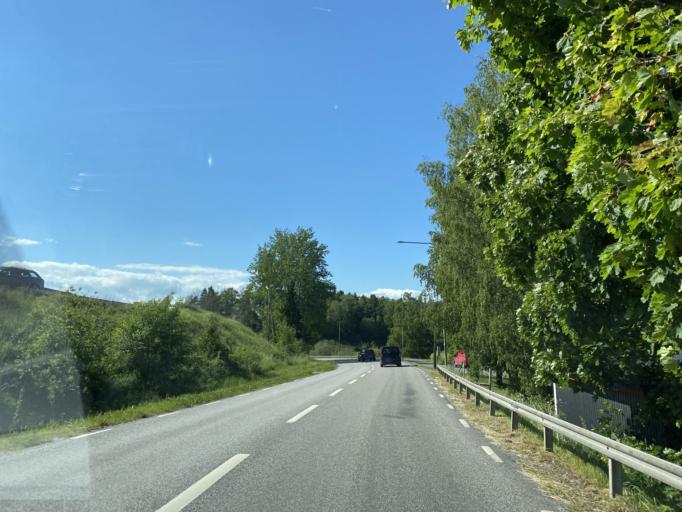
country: SE
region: Stockholm
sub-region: Norrtalje Kommun
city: Norrtalje
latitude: 59.7692
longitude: 18.6871
